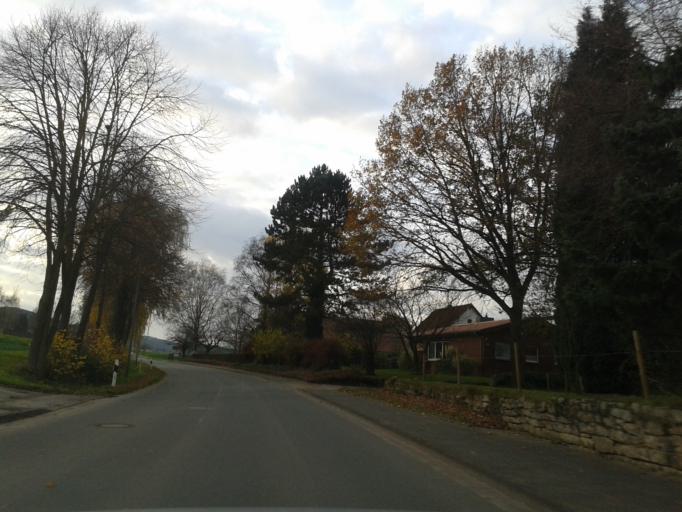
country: DE
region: North Rhine-Westphalia
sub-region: Regierungsbezirk Detmold
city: Blomberg
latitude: 51.9135
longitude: 9.0547
